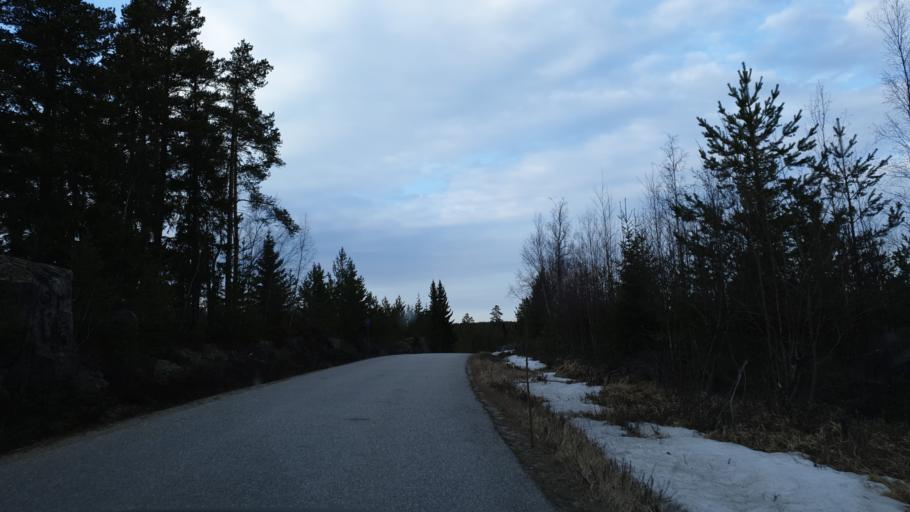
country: SE
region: Vaesternorrland
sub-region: Sundsvalls Kommun
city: Njurundabommen
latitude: 62.0274
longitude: 17.4035
